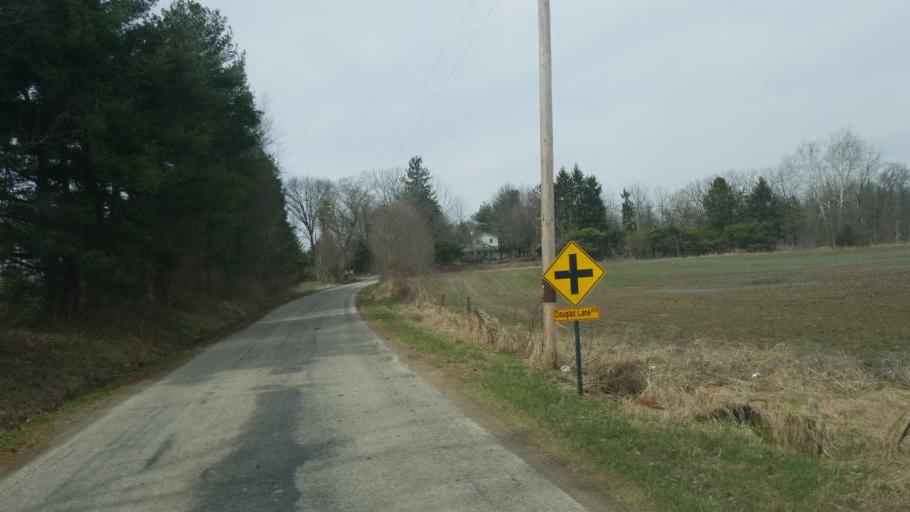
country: US
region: Ohio
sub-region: Licking County
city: Utica
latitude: 40.2466
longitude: -82.5767
